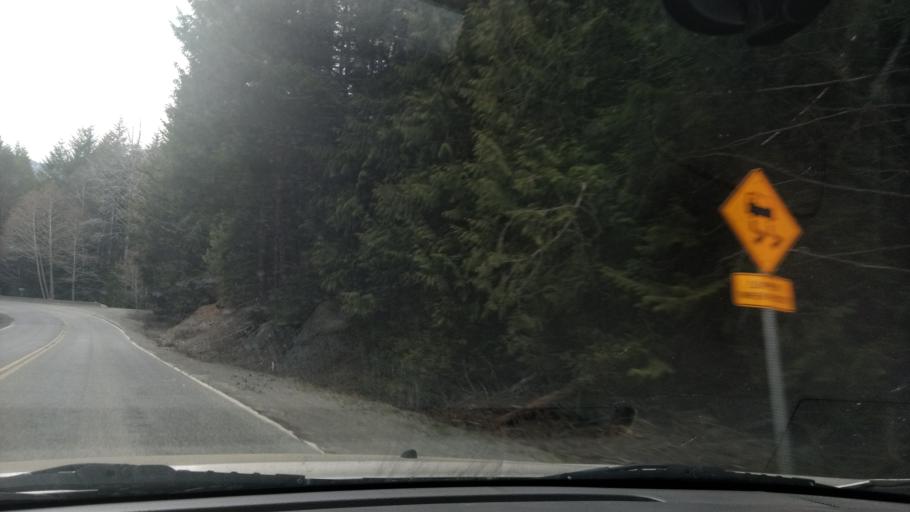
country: CA
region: British Columbia
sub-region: Regional District of Alberni-Clayoquot
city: Tofino
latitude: 49.8400
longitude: -125.9271
